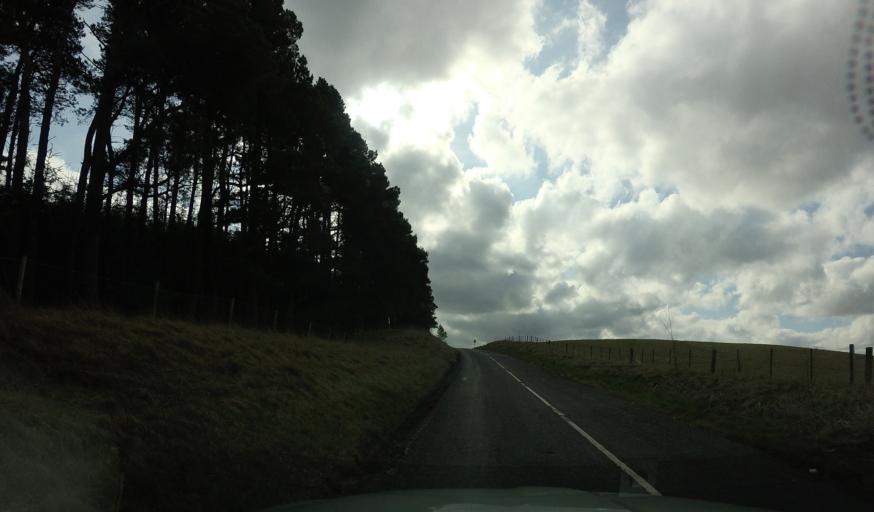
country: GB
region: Scotland
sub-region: Midlothian
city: Loanhead
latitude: 55.7953
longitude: -3.1451
